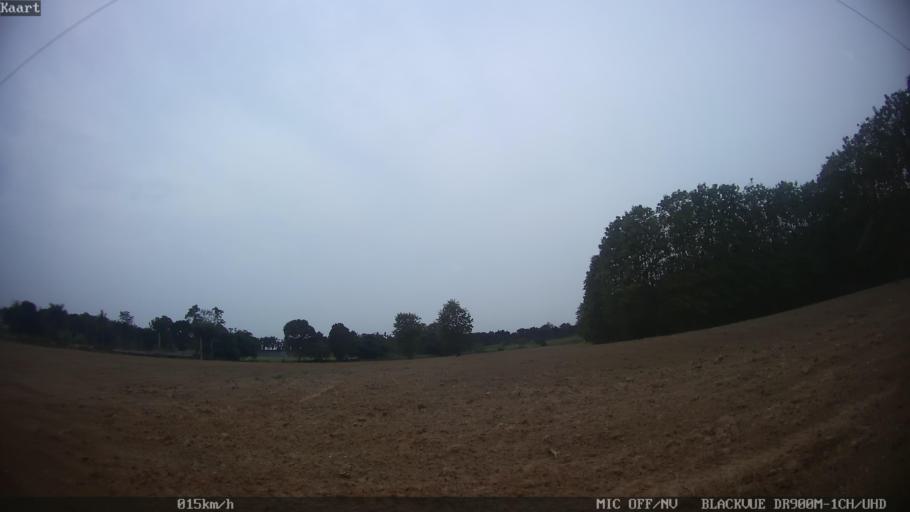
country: ID
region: Lampung
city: Panjang
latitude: -5.4060
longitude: 105.3576
